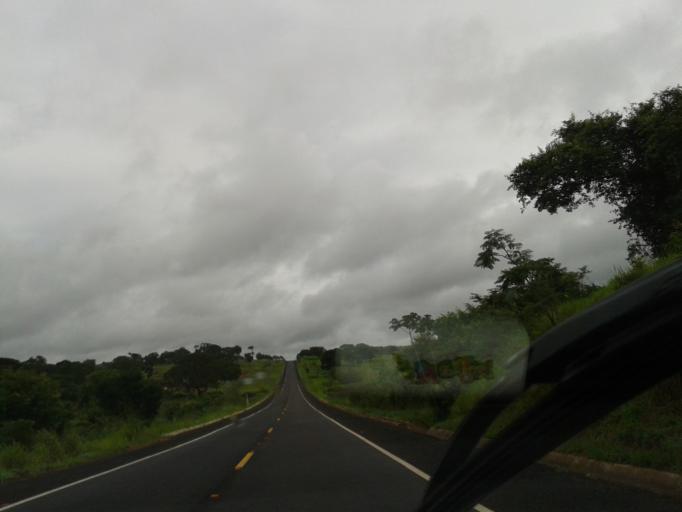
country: BR
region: Minas Gerais
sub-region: Santa Vitoria
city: Santa Vitoria
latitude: -19.2408
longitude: -50.0149
